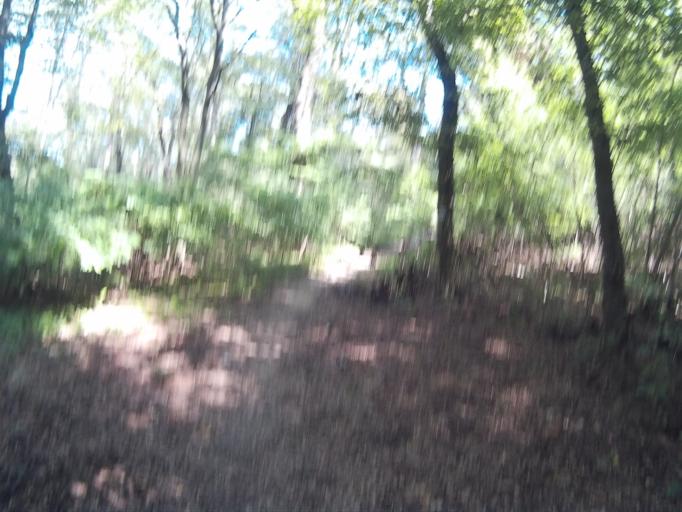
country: HU
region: Vas
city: Gencsapati
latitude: 47.2393
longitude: 16.5644
